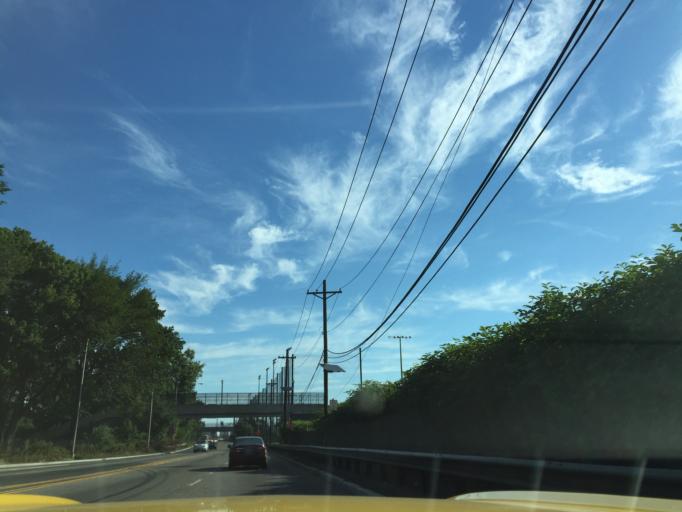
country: US
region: New Jersey
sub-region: Hudson County
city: Jersey City
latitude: 40.7248
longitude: -74.0891
